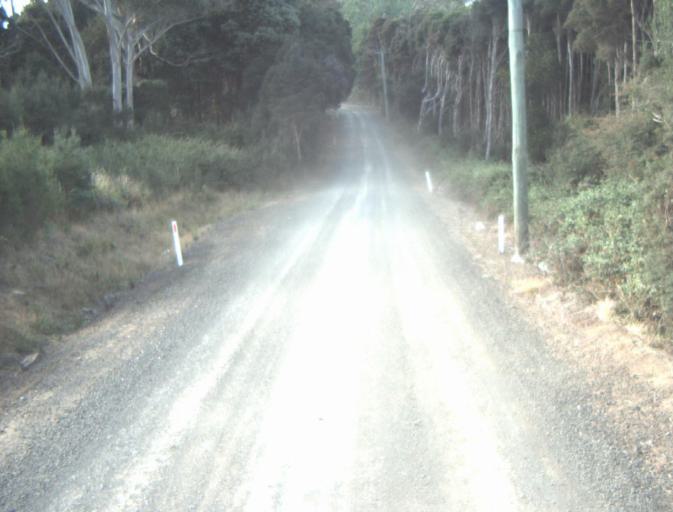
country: AU
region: Tasmania
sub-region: Launceston
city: Mayfield
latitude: -41.2734
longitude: 147.1837
